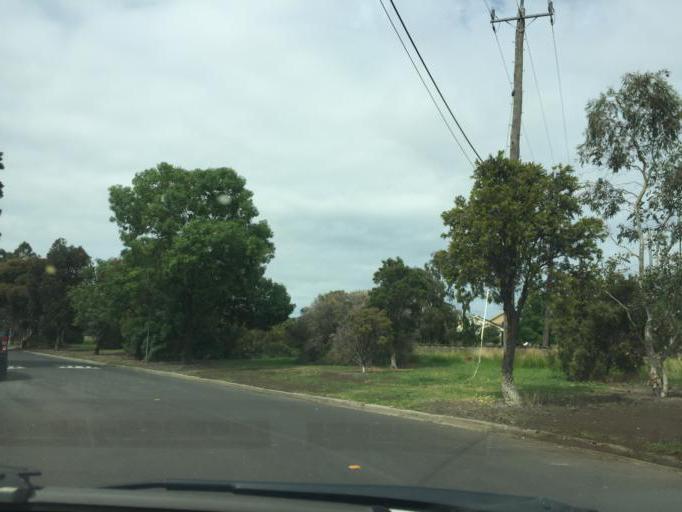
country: AU
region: Victoria
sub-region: Hobsons Bay
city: South Kingsville
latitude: -37.8269
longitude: 144.8714
